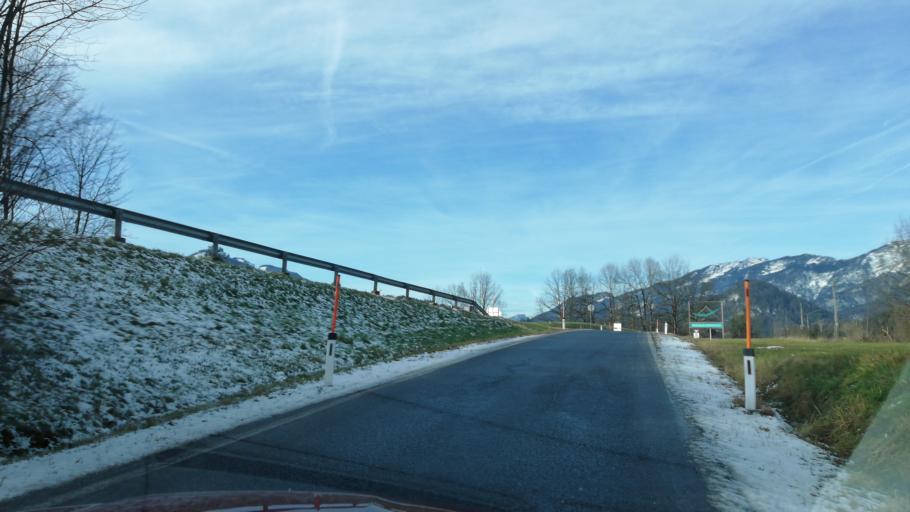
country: AT
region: Upper Austria
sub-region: Politischer Bezirk Kirchdorf an der Krems
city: Rossleithen
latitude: 47.7153
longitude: 14.3147
